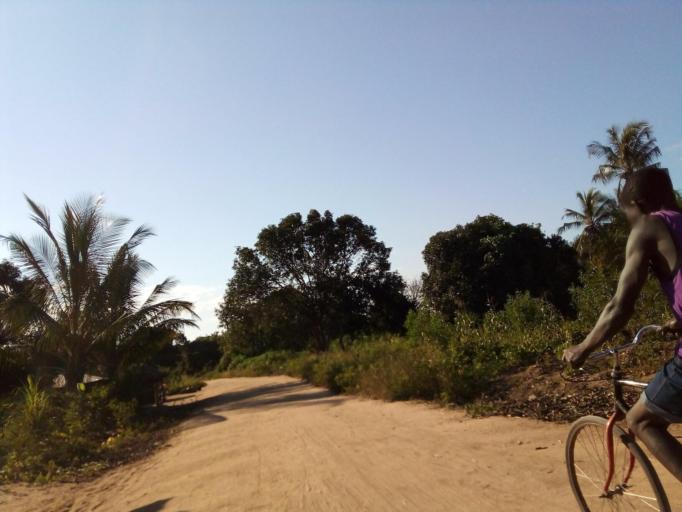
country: MZ
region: Zambezia
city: Quelimane
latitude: -17.5183
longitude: 36.6860
